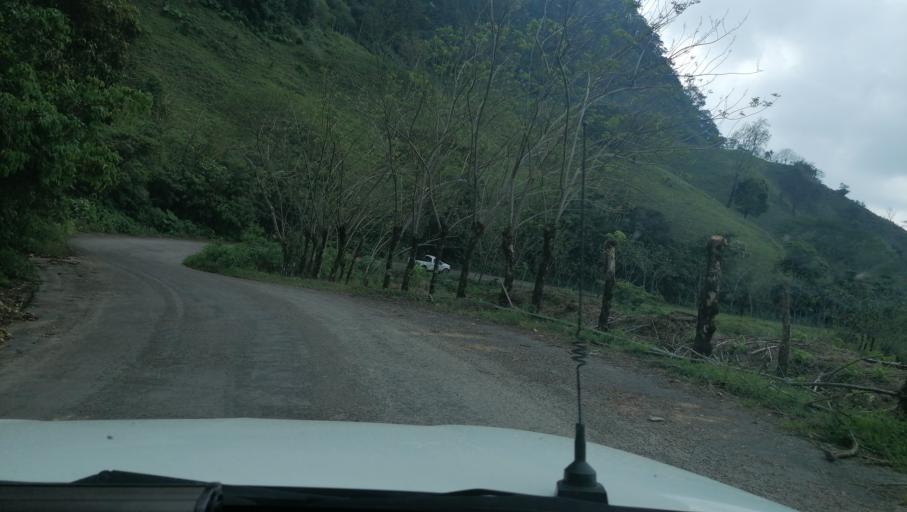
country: MX
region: Chiapas
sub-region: Francisco Leon
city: San Miguel la Sardina
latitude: 17.2457
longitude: -93.2870
